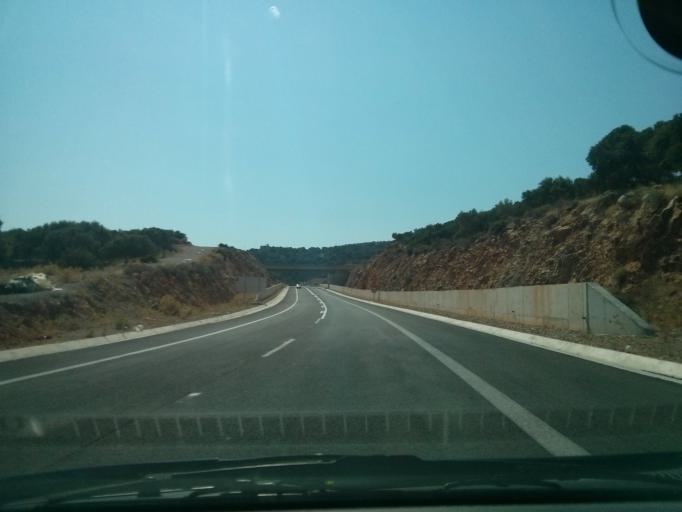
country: GR
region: Crete
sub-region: Nomos Lasithiou
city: Agios Nikolaos
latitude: 35.1661
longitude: 25.7036
